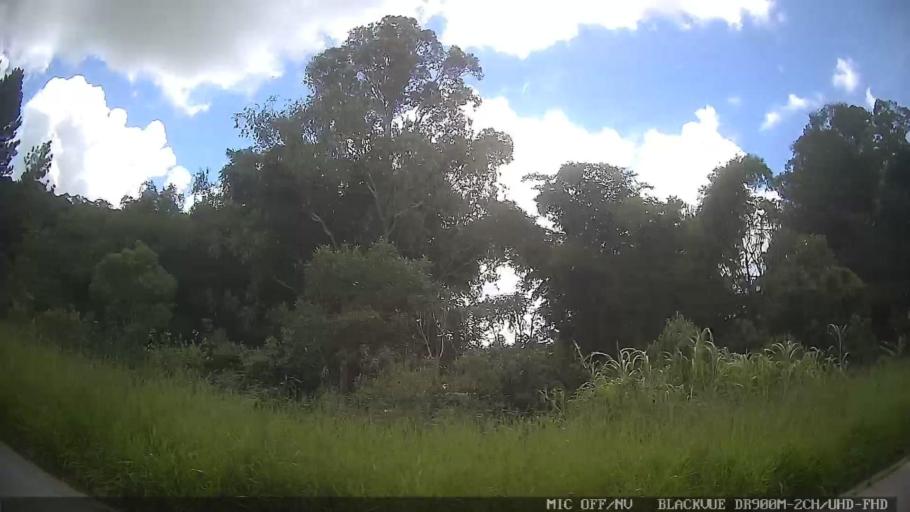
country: BR
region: Sao Paulo
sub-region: Amparo
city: Amparo
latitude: -22.7808
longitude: -46.7316
